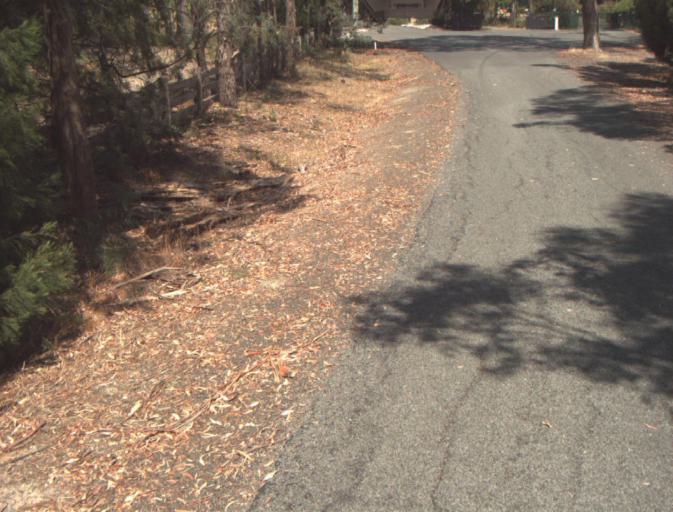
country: AU
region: Tasmania
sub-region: Launceston
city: Newstead
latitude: -41.4922
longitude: 147.1954
